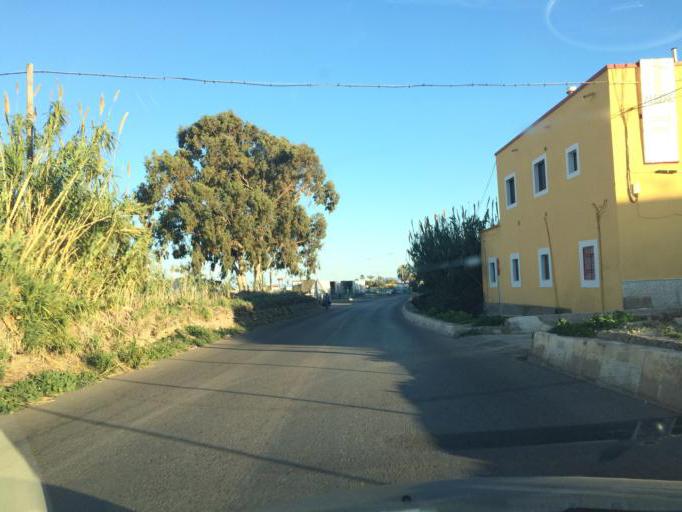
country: ES
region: Andalusia
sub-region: Provincia de Almeria
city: Almeria
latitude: 36.8407
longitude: -2.4236
